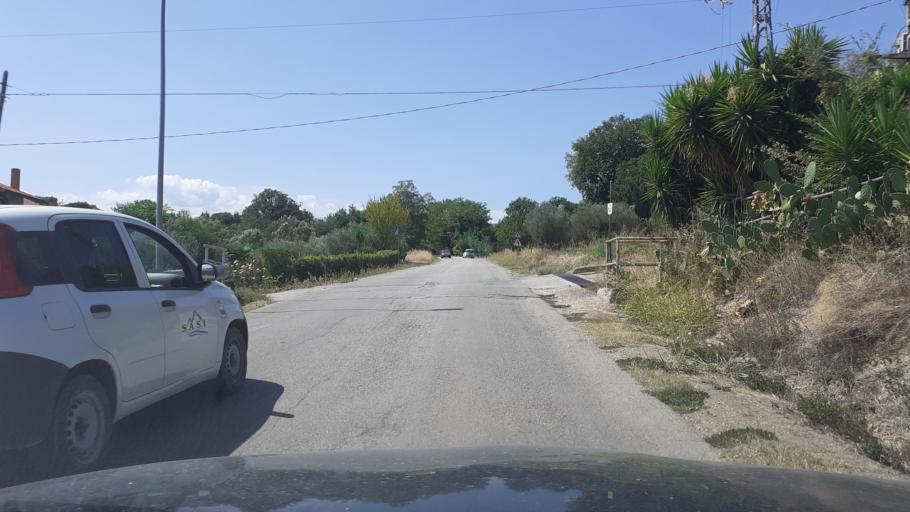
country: IT
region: Abruzzo
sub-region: Provincia di Chieti
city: Santa Maria Imbaro
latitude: 42.2155
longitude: 14.4630
